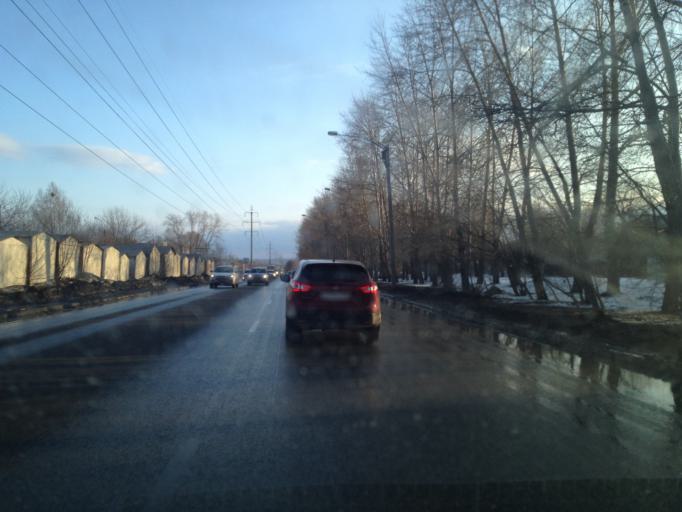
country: RU
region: Sverdlovsk
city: Sovkhoznyy
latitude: 56.7685
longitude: 60.5947
